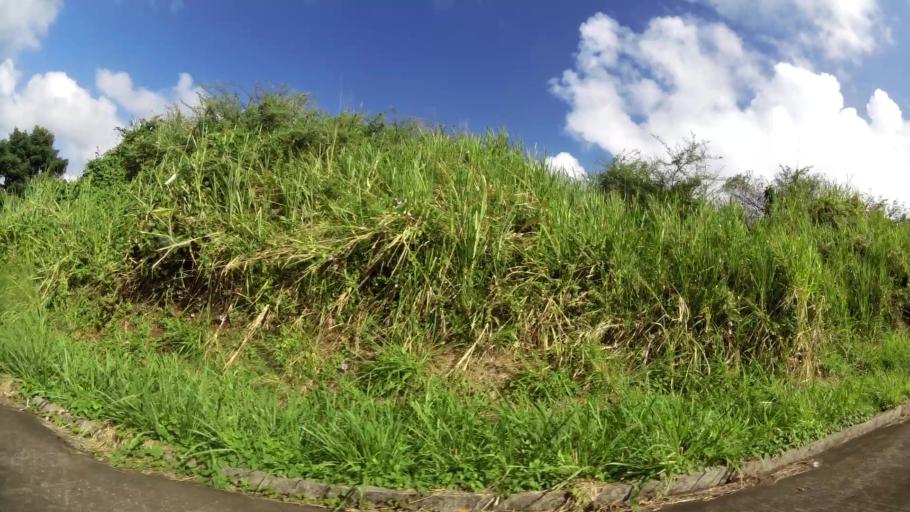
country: MQ
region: Martinique
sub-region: Martinique
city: Sainte-Marie
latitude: 14.8051
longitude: -61.0113
